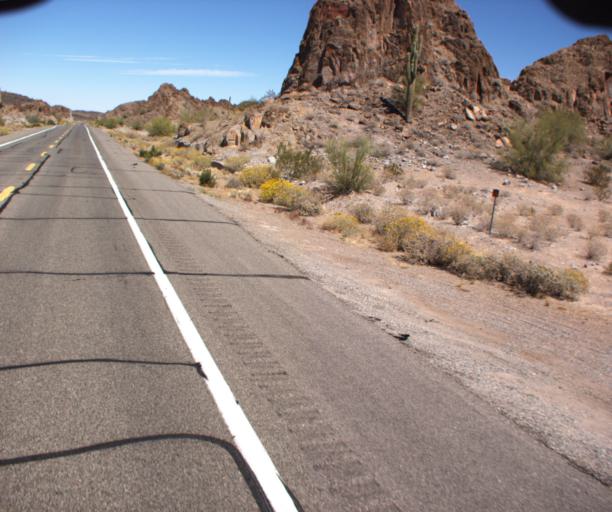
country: US
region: Arizona
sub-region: Pima County
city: Ajo
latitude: 32.5443
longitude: -112.8800
